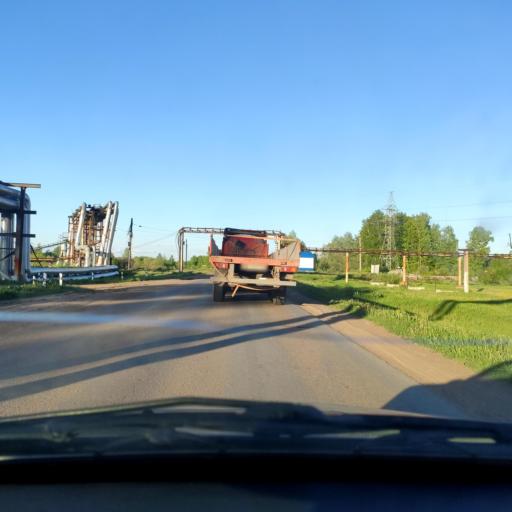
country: RU
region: Bashkortostan
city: Blagoveshchensk
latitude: 55.0298
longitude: 56.0701
